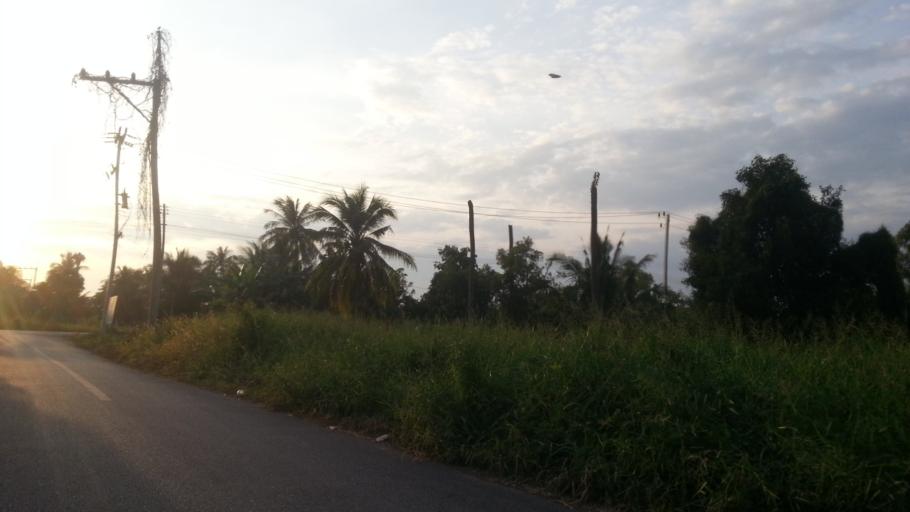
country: TH
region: Pathum Thani
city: Ban Rangsit
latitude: 14.0409
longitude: 100.8482
